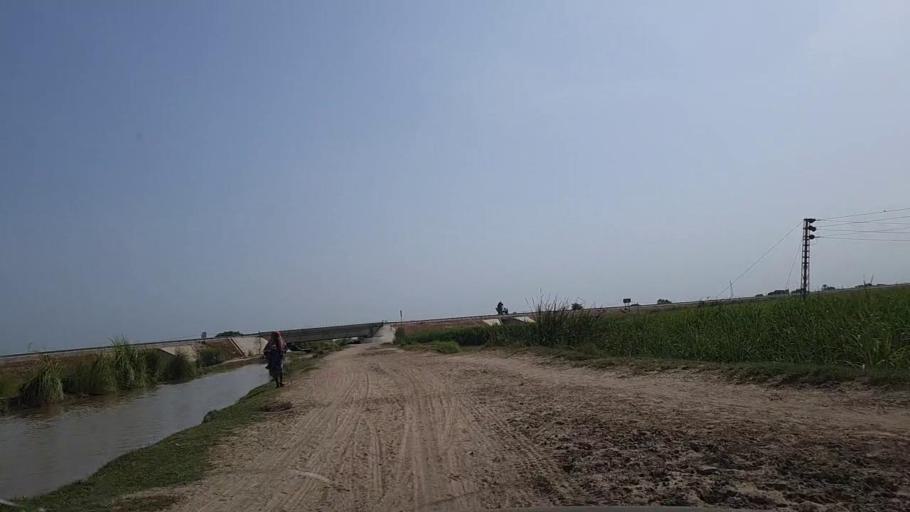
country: PK
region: Sindh
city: Ghotki
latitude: 28.0646
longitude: 69.3829
